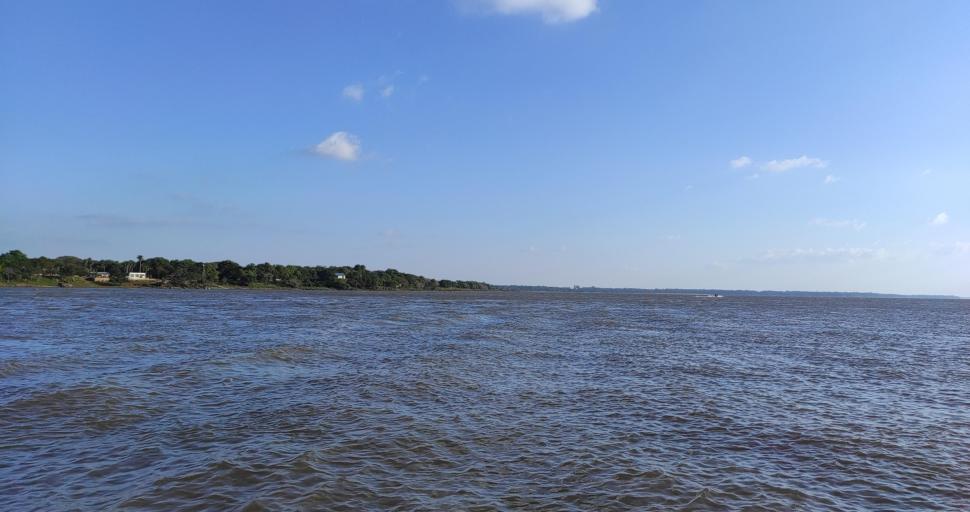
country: AR
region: Corrientes
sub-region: Departamento de Itati
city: Itati
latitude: -27.2615
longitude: -58.2669
